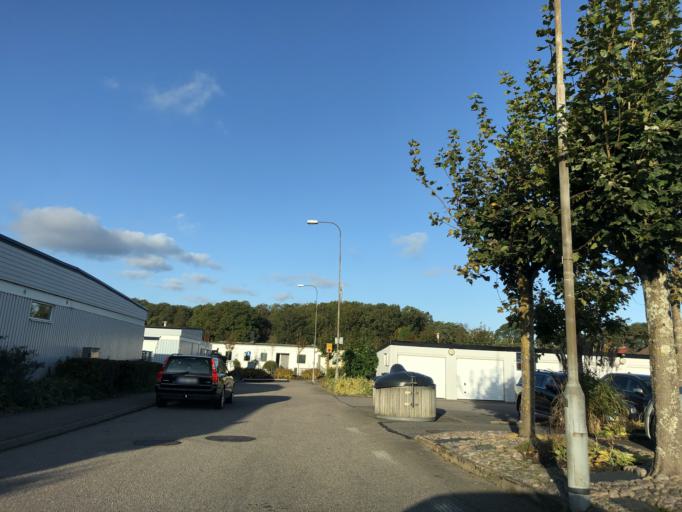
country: SE
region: Vaestra Goetaland
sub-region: Goteborg
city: Majorna
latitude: 57.6578
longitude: 11.8790
